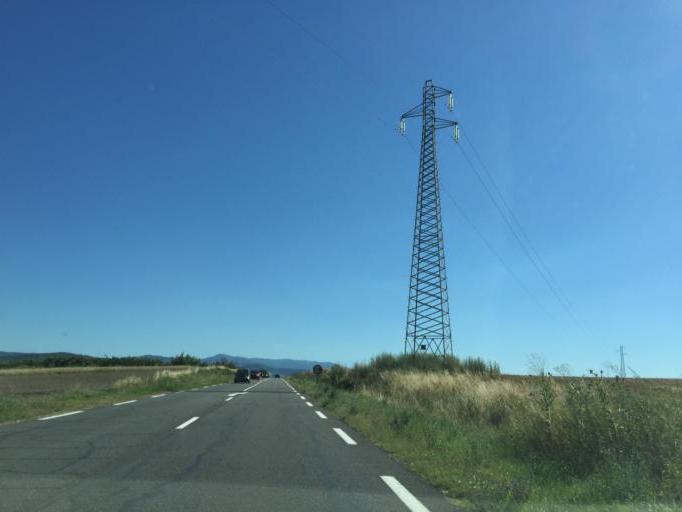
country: FR
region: Rhone-Alpes
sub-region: Departement du Rhone
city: Saint-Maurice-sur-Dargoire
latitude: 45.5635
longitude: 4.6428
